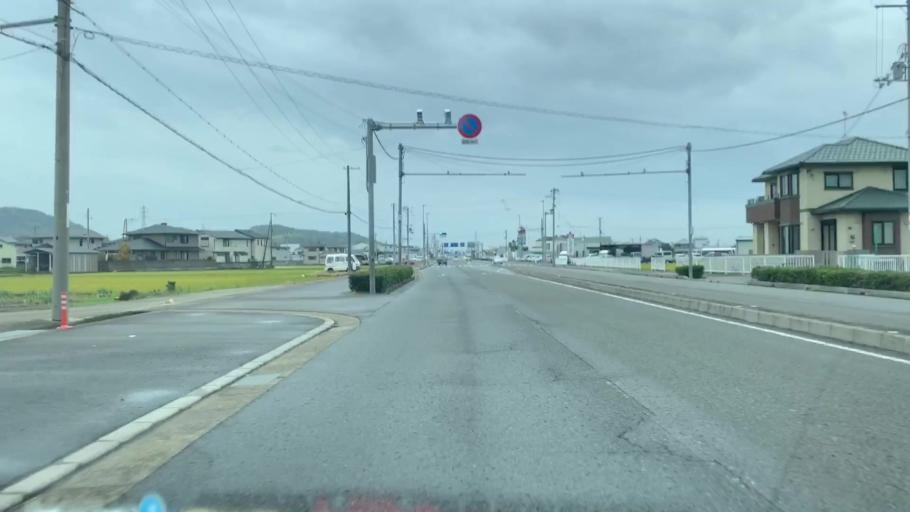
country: JP
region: Wakayama
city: Wakayama-shi
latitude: 34.2386
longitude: 135.2383
